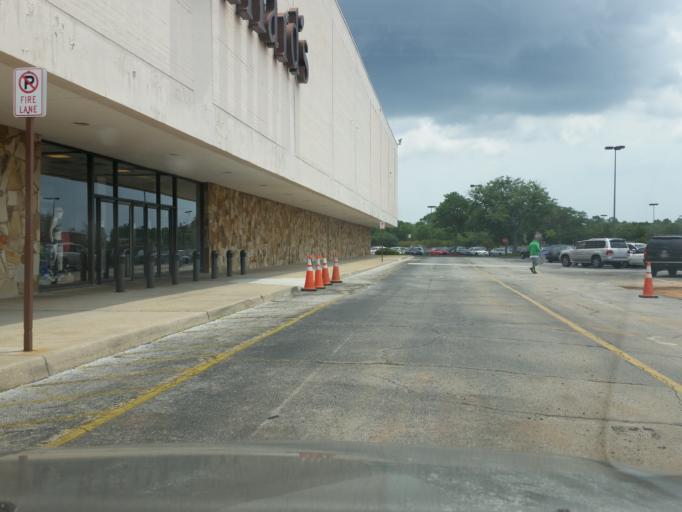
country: US
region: Florida
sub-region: Escambia County
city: Brent
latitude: 30.4741
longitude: -87.2093
